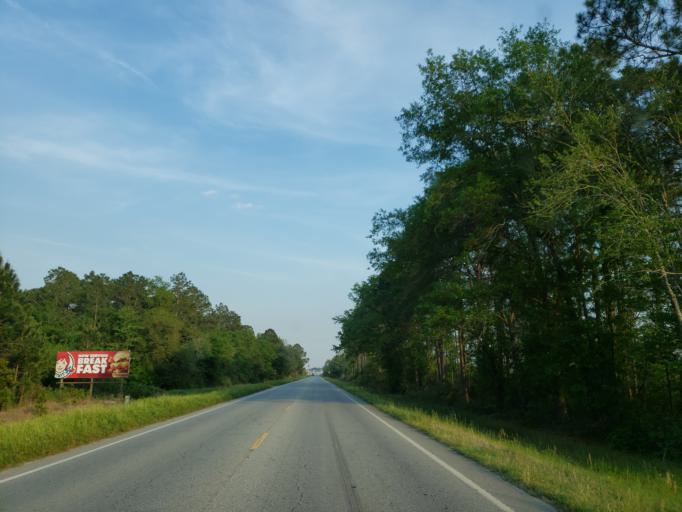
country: US
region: Georgia
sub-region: Cook County
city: Sparks
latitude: 31.1451
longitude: -83.4559
